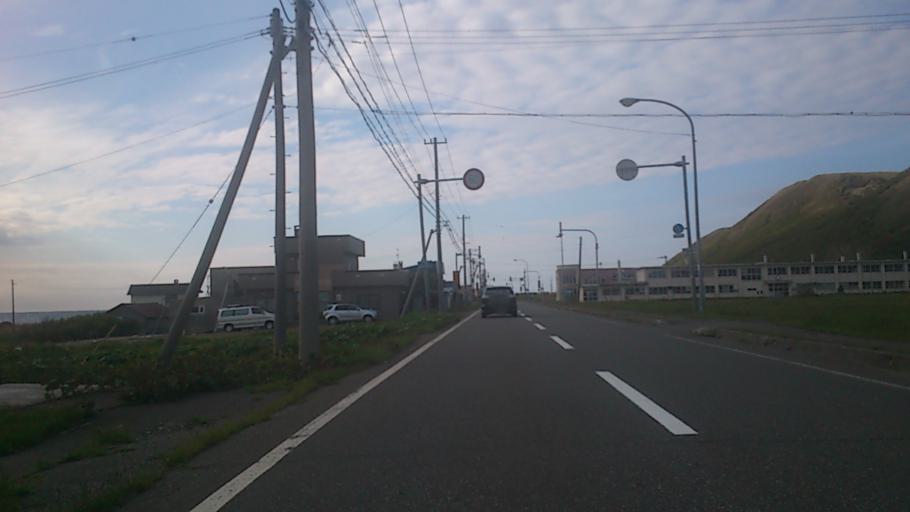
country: JP
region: Hokkaido
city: Wakkanai
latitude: 45.3952
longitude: 141.6384
